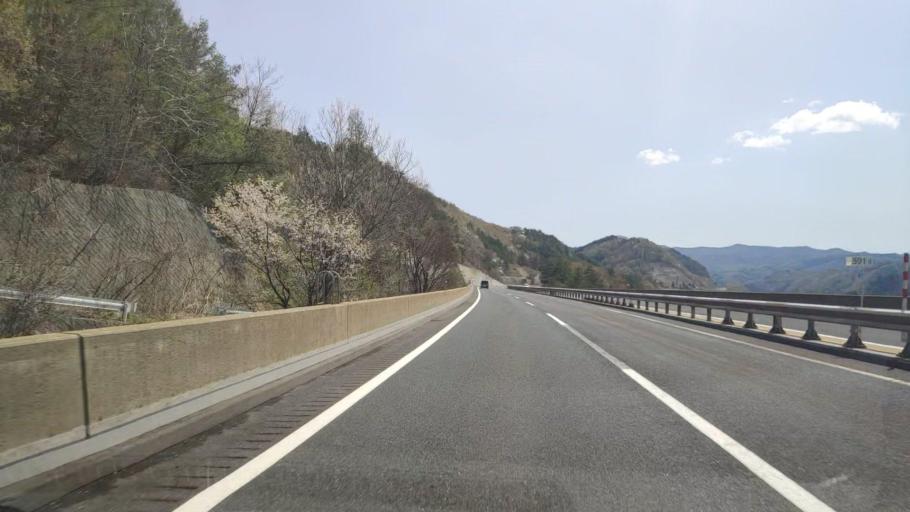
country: JP
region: Iwate
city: Ichinohe
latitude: 40.2299
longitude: 141.3165
